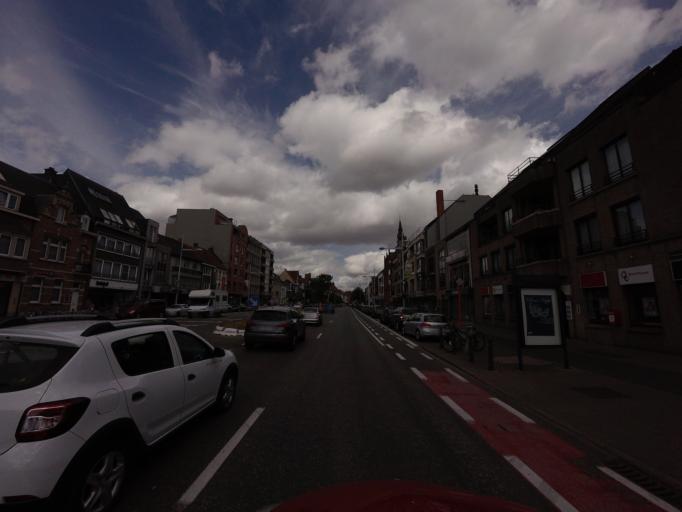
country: BE
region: Flanders
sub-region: Provincie Oost-Vlaanderen
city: Eeklo
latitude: 51.1832
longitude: 3.5693
